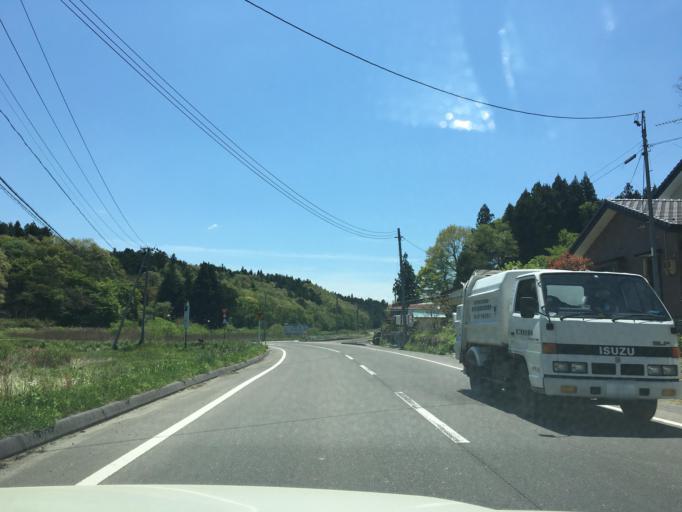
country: JP
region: Fukushima
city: Funehikimachi-funehiki
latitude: 37.3169
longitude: 140.6223
